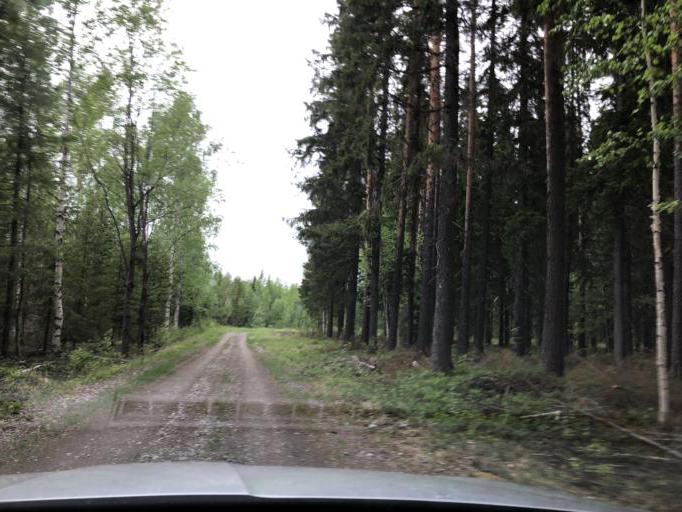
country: SE
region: Norrbotten
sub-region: Pitea Kommun
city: Roknas
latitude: 65.3990
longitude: 21.2645
